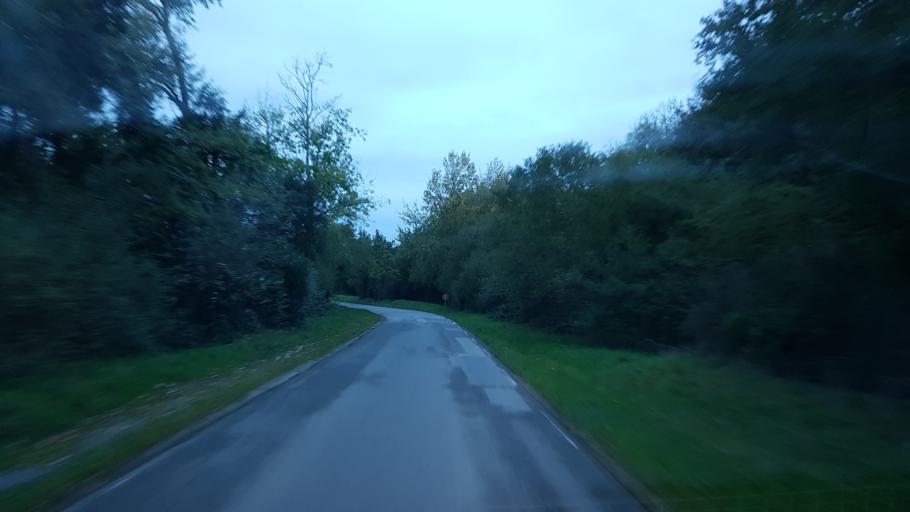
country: FR
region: Brittany
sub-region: Departement du Morbihan
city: Sarzeau
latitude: 47.5307
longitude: -2.7737
